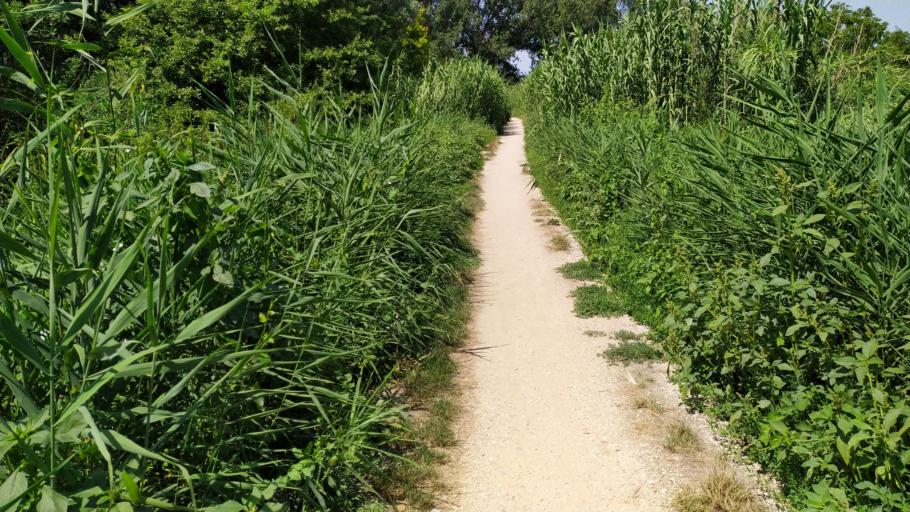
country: IT
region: Emilia-Romagna
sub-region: Forli-Cesena
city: Forli
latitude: 44.2107
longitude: 12.0227
